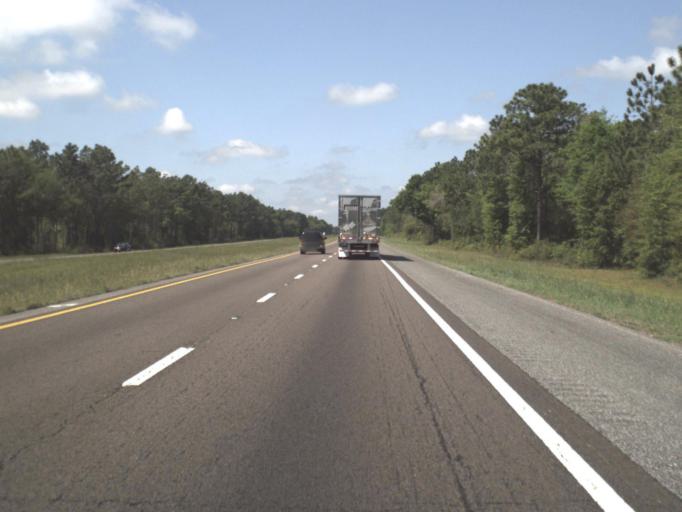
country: US
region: Florida
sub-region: Santa Rosa County
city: East Milton
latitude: 30.6482
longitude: -86.8947
